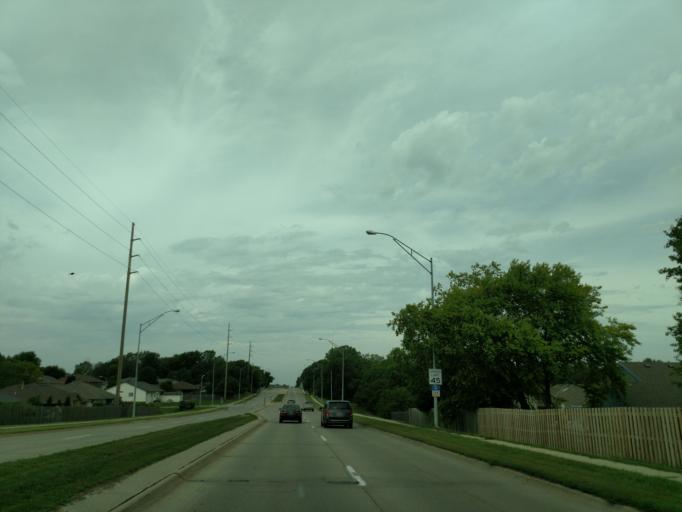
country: US
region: Nebraska
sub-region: Douglas County
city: Ralston
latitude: 41.1909
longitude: -96.0537
